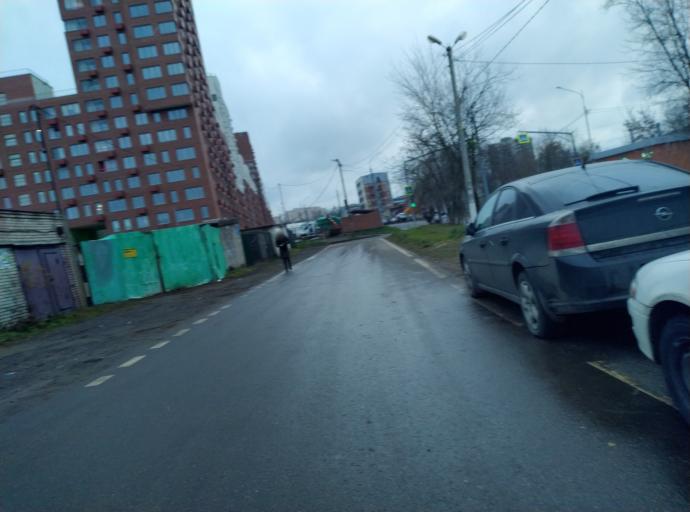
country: RU
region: Moskovskaya
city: Korenevo
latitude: 55.6668
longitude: 37.9981
